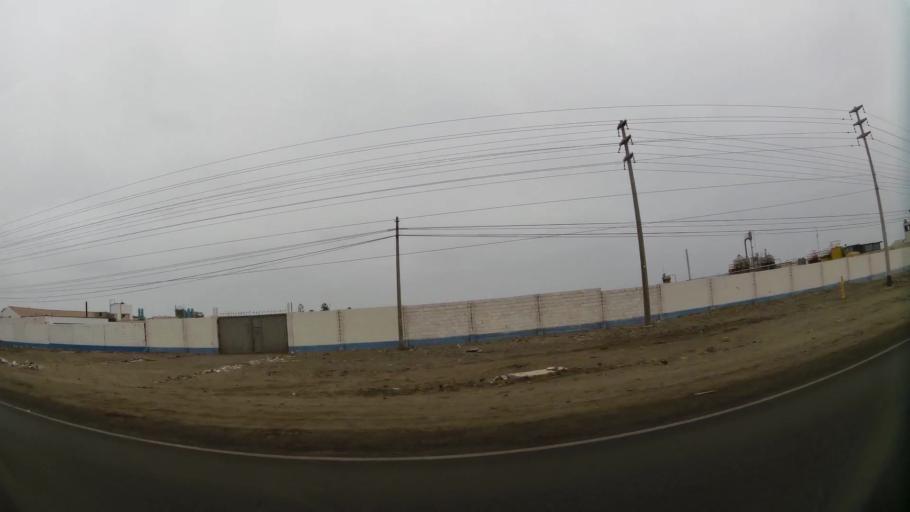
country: PE
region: Ica
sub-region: Provincia de Pisco
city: Paracas
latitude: -13.7962
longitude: -76.2402
